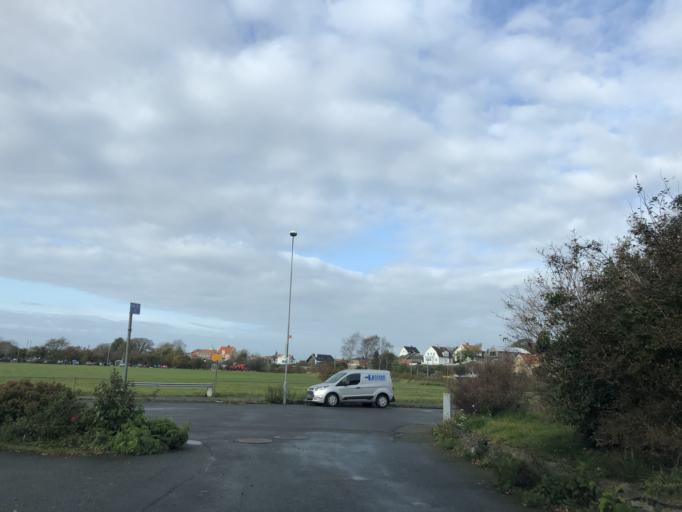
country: SE
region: Vaestra Goetaland
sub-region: Goteborg
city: Majorna
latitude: 57.6682
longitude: 11.8589
